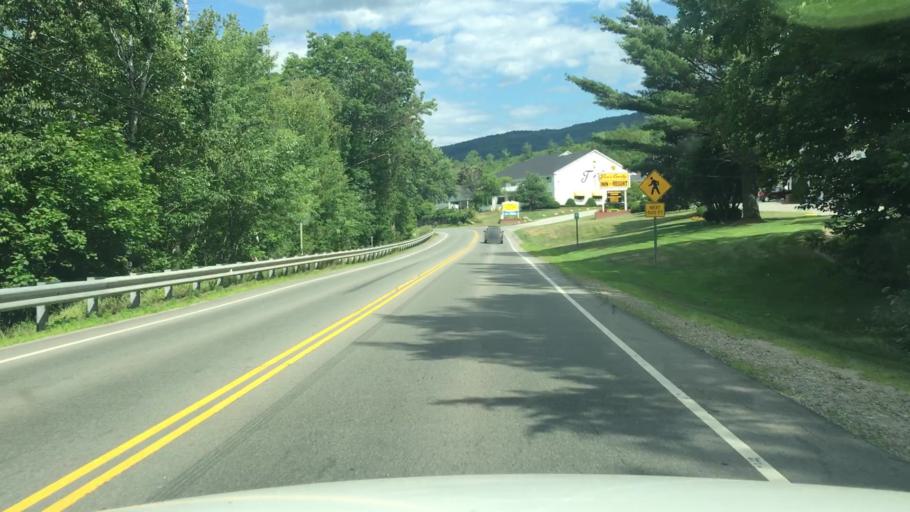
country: US
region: New Hampshire
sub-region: Coos County
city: Gorham
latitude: 44.3853
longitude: -71.1599
